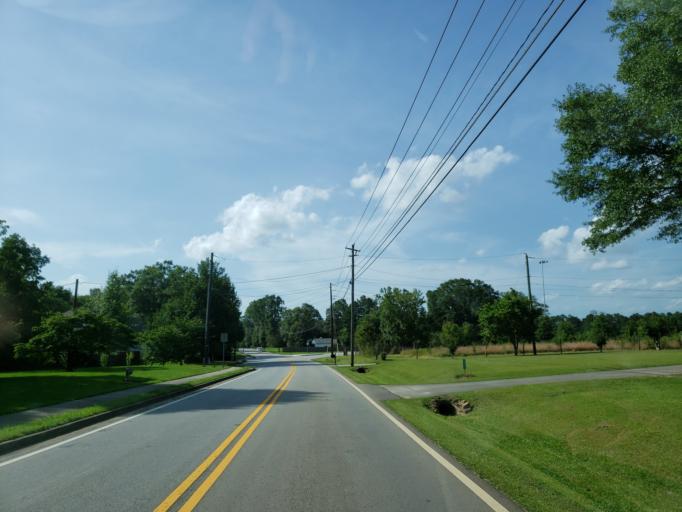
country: US
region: Georgia
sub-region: Cobb County
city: Powder Springs
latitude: 33.8907
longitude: -84.6846
